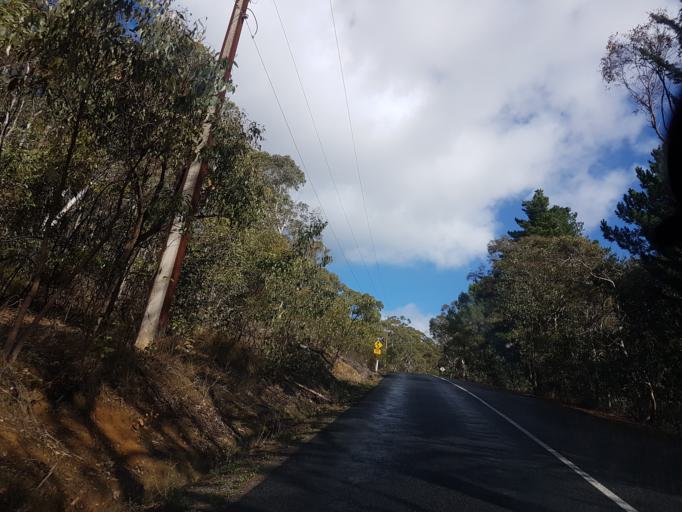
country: AU
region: South Australia
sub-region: Adelaide Hills
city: Heathfield
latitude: -35.0446
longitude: 138.7051
